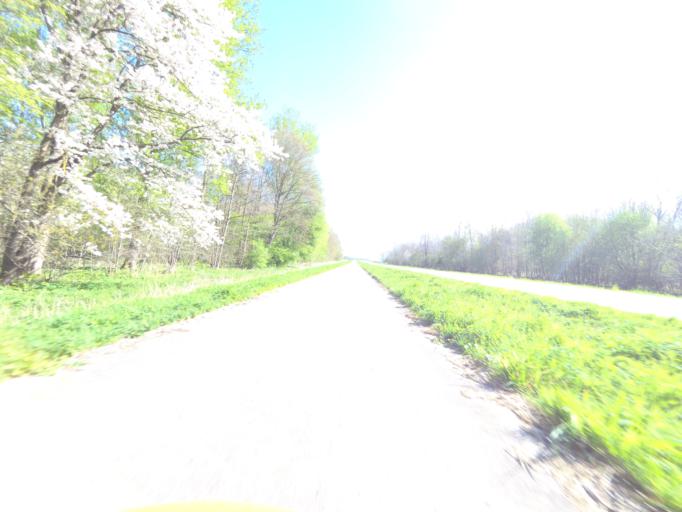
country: NL
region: Gelderland
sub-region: Gemeente Harderwijk
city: Harderwijk
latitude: 52.4364
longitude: 5.5673
